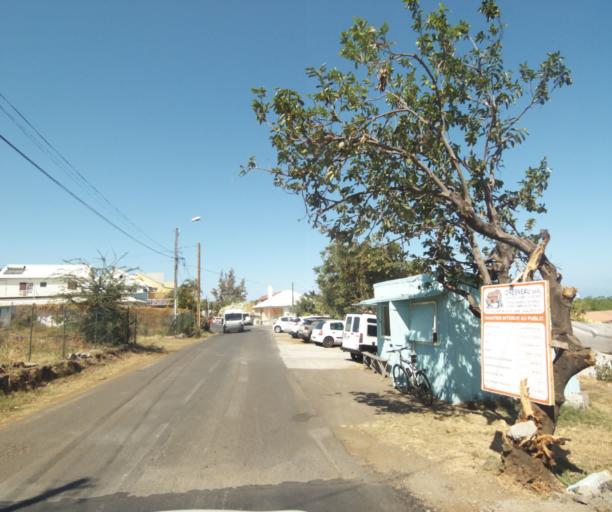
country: RE
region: Reunion
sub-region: Reunion
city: La Possession
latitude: -20.9807
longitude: 55.3279
